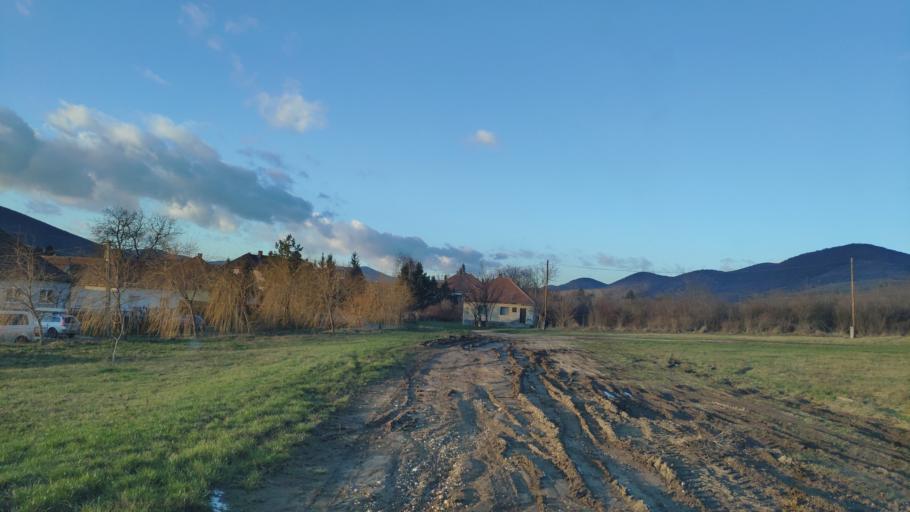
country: HU
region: Borsod-Abauj-Zemplen
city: Tolcsva
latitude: 48.2813
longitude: 21.4571
